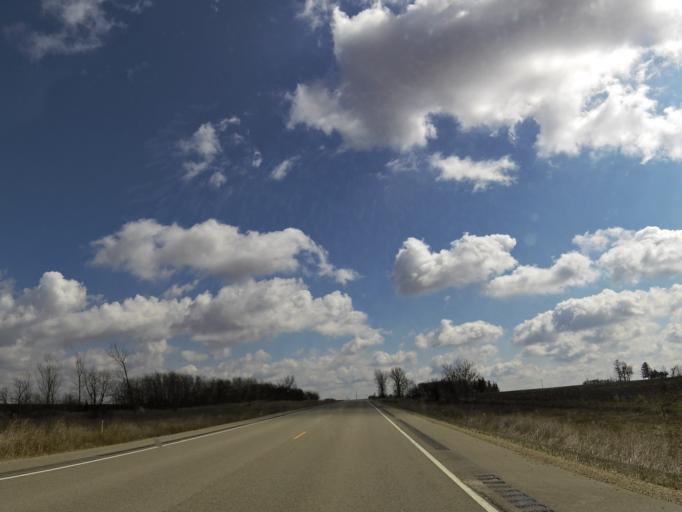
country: US
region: Minnesota
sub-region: Goodhue County
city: Kenyon
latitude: 44.2445
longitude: -92.9620
